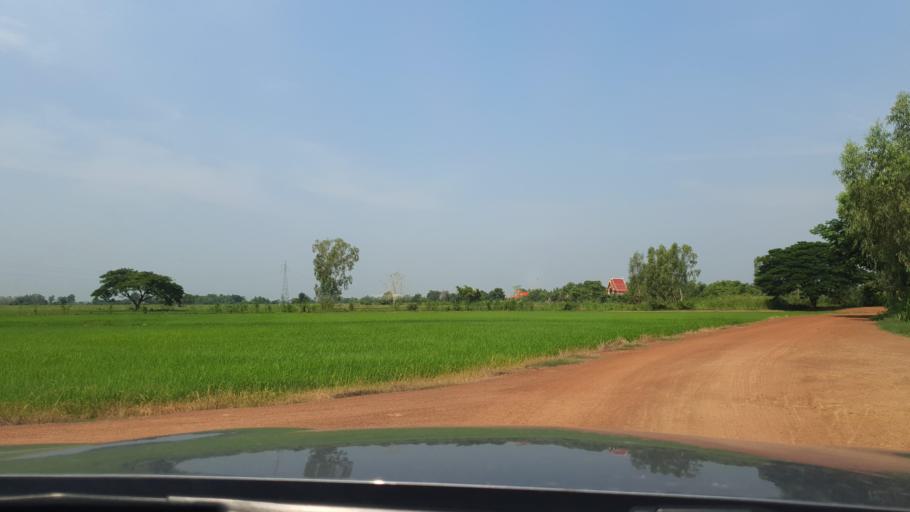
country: TH
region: Phitsanulok
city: Bang Rakam
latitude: 16.7841
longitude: 100.1074
